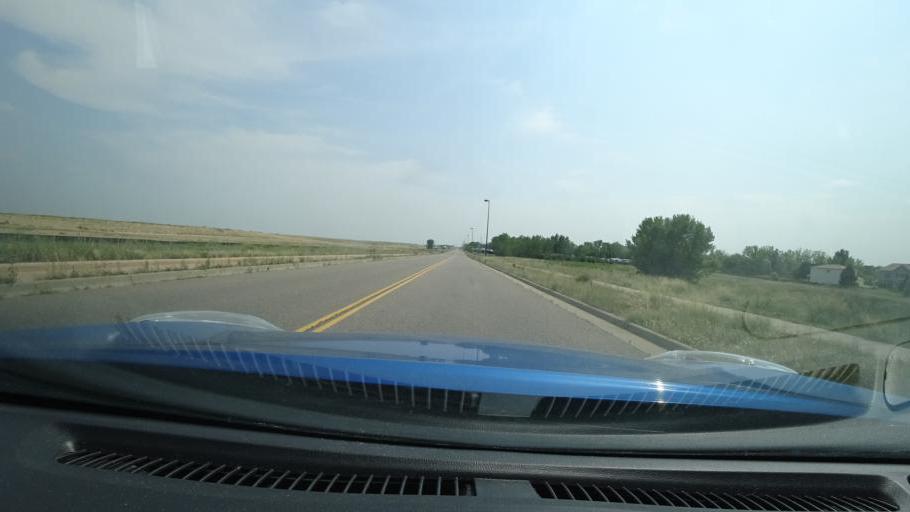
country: US
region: Colorado
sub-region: Adams County
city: Aurora
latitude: 39.7793
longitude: -104.7346
